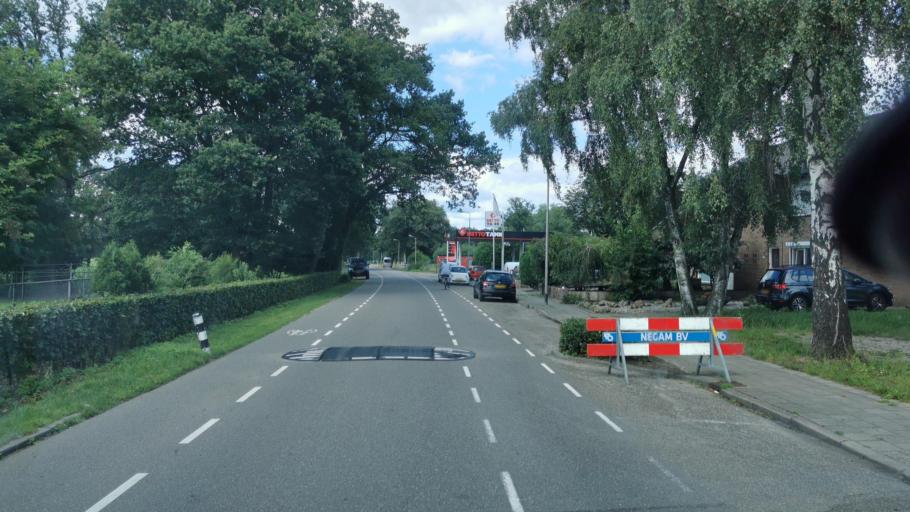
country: NL
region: Overijssel
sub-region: Gemeente Losser
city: Losser
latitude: 52.2341
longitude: 7.0035
